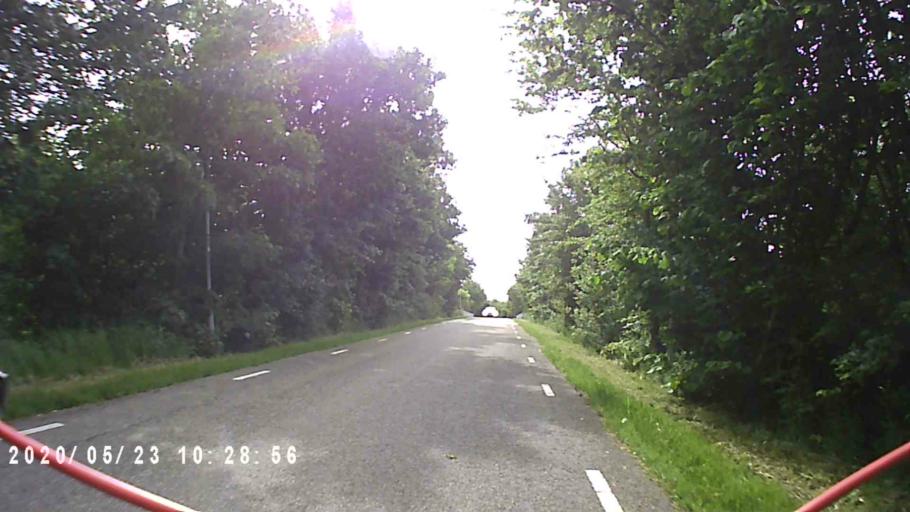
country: NL
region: Groningen
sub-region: Gemeente Appingedam
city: Appingedam
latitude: 53.3006
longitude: 6.8545
